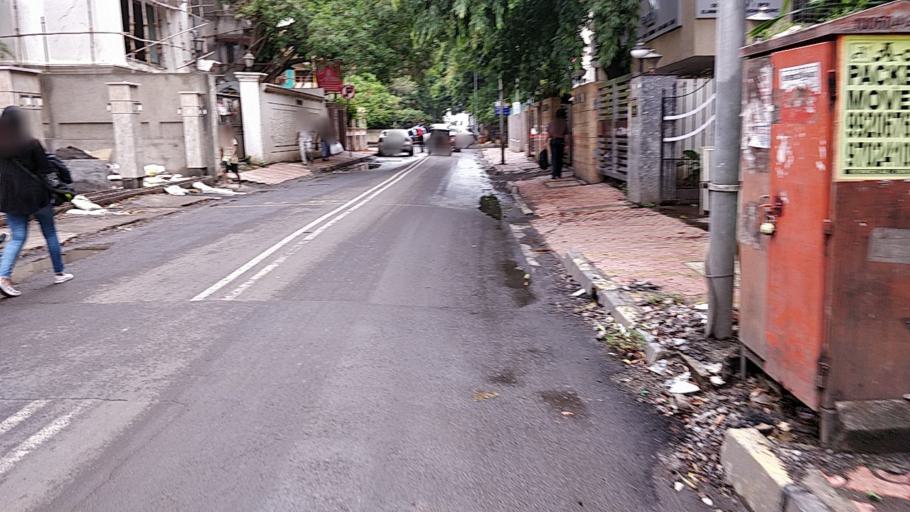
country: IN
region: Maharashtra
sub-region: Mumbai Suburban
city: Mumbai
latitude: 19.0700
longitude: 72.8360
